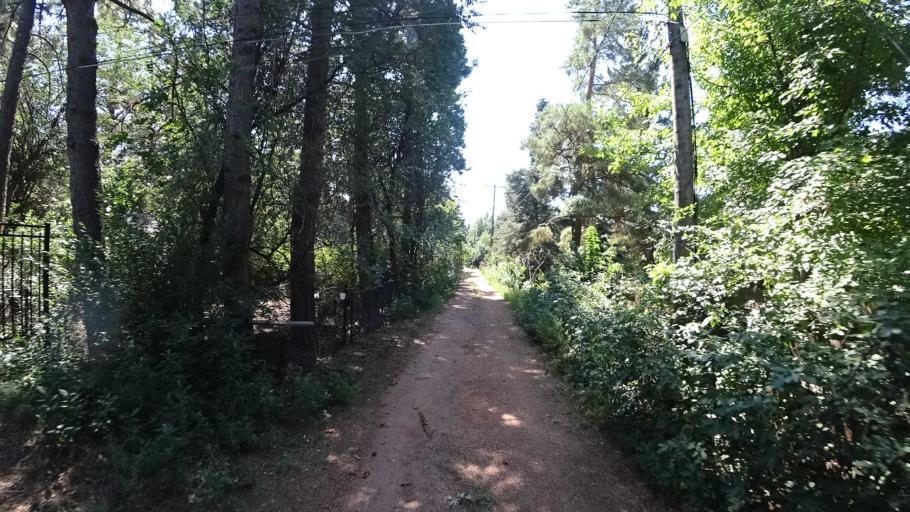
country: US
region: Colorado
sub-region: El Paso County
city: Colorado Springs
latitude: 38.8573
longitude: -104.8283
